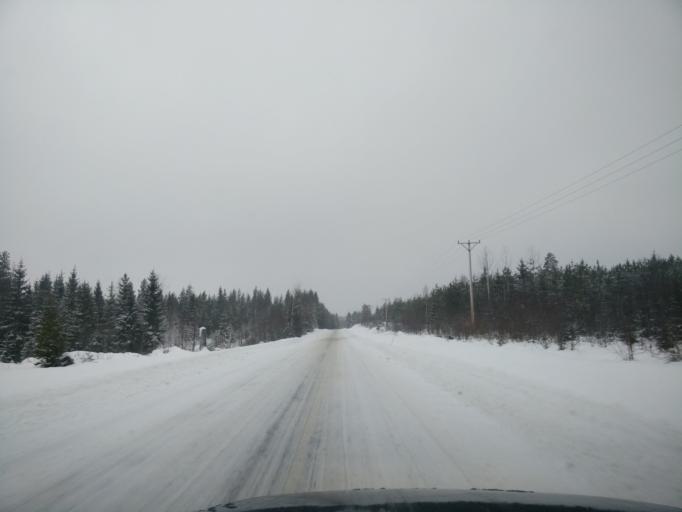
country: SE
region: Vaesternorrland
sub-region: Ange Kommun
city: Ange
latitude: 62.4660
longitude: 15.4504
